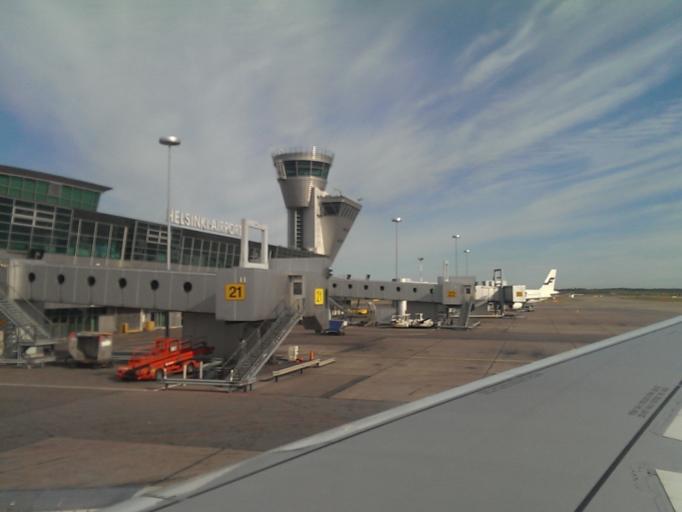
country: FI
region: Uusimaa
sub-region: Helsinki
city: Vantaa
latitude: 60.3187
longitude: 24.9699
